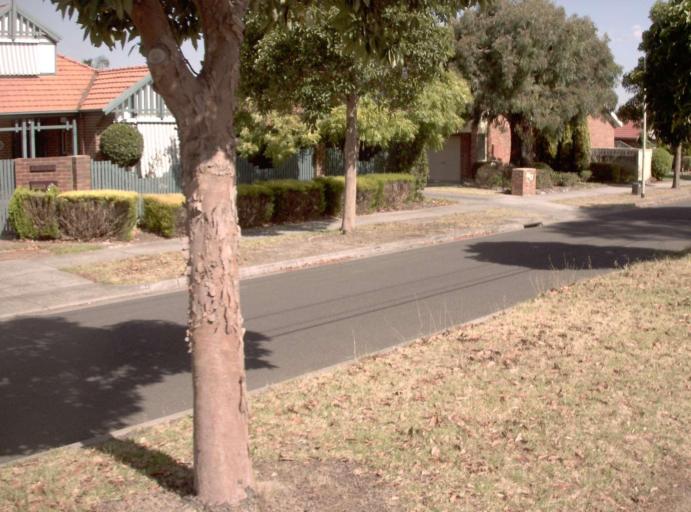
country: AU
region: Victoria
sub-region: Monash
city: Mulgrave
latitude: -37.9150
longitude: 145.1876
